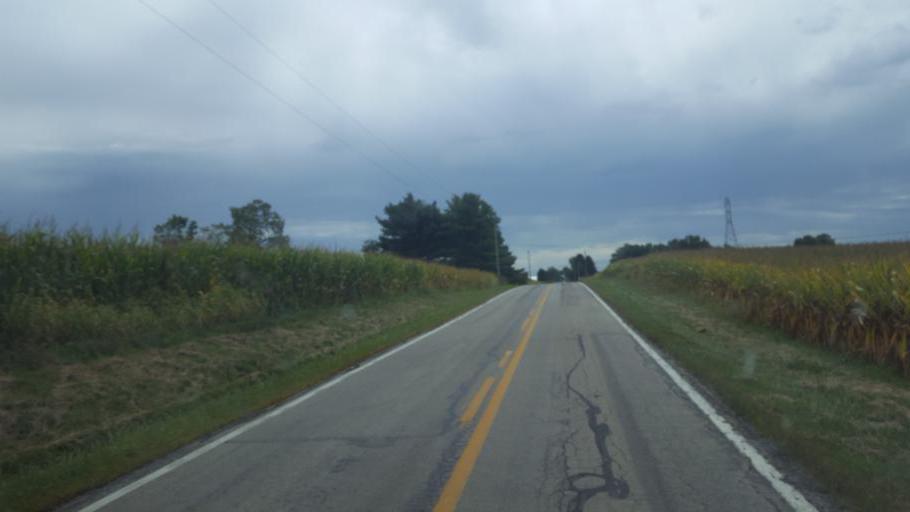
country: US
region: Ohio
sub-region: Knox County
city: Centerburg
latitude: 40.2738
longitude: -82.7510
